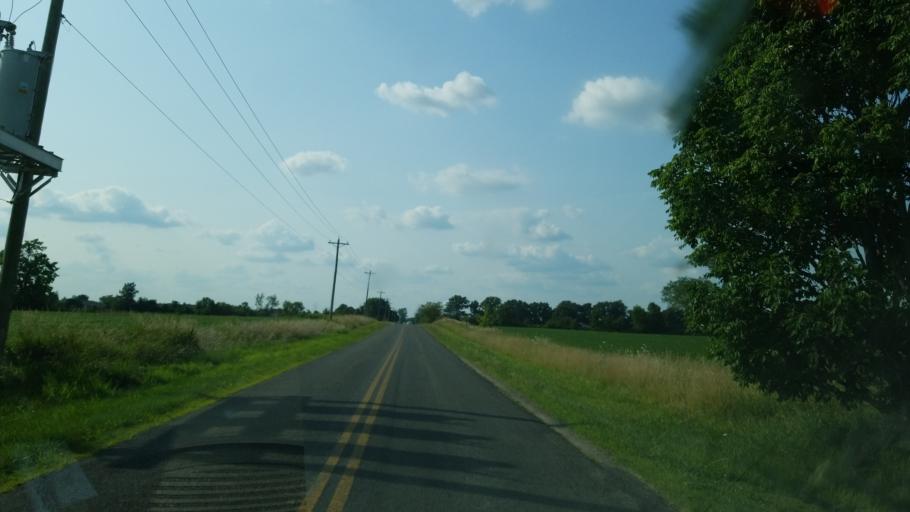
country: US
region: Ohio
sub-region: Union County
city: New California
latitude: 40.1733
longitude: -83.2763
